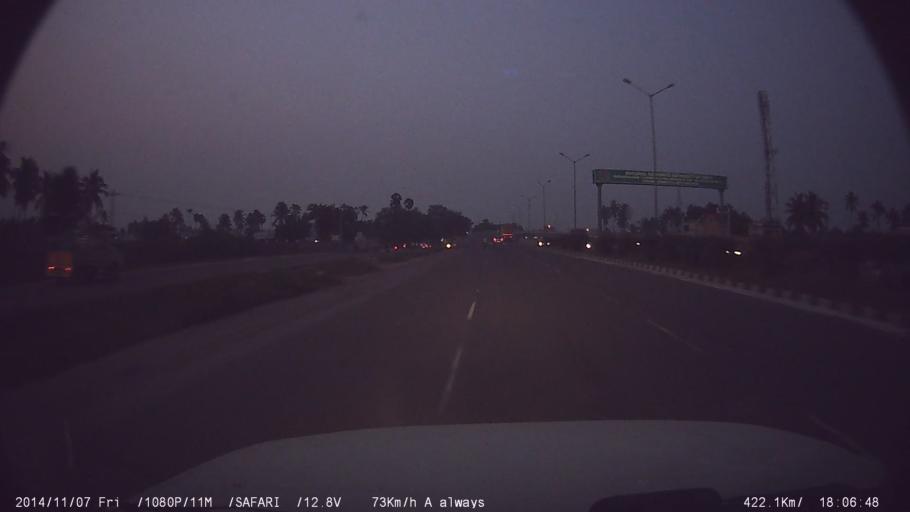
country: IN
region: Tamil Nadu
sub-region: Erode
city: Bhavani
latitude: 11.4251
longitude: 77.6759
